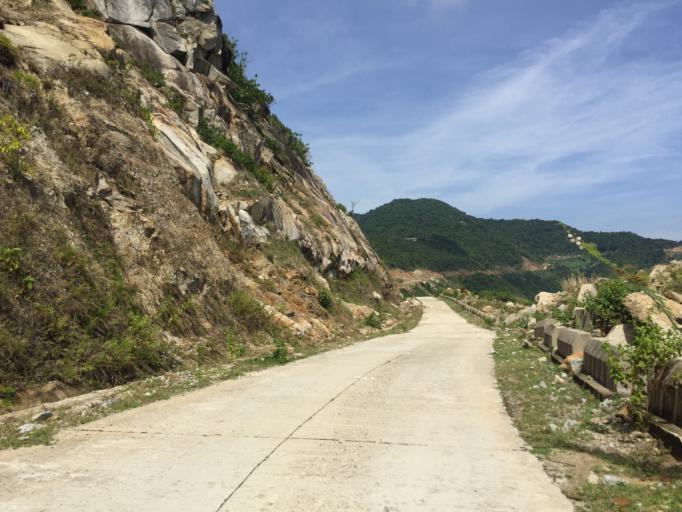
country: VN
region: Quang Nam
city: Hoi An
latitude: 15.9615
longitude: 108.5155
